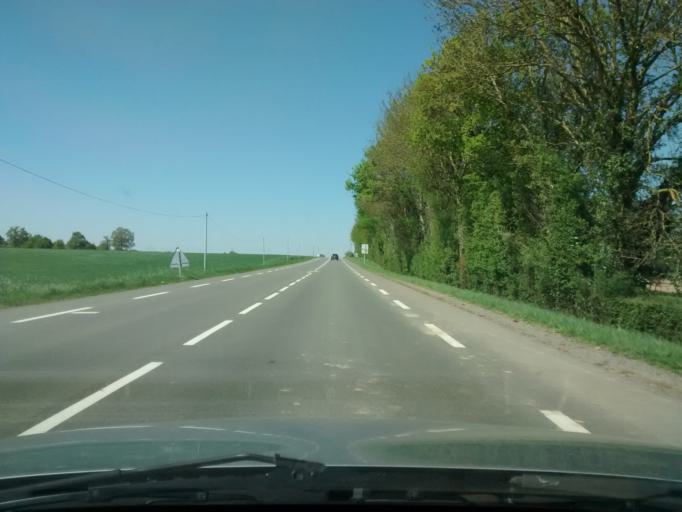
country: FR
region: Pays de la Loire
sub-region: Departement de la Mayenne
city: Vaiges
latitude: 48.0375
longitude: -0.4514
